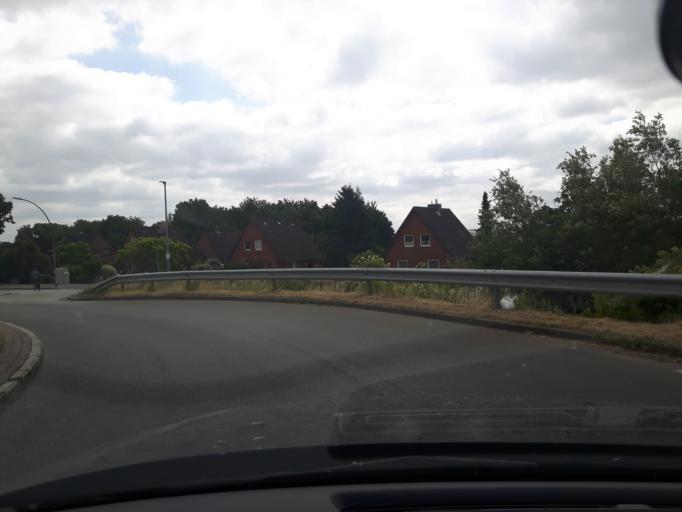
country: DE
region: Schleswig-Holstein
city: Sierksdorf
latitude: 54.0936
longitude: 10.7842
